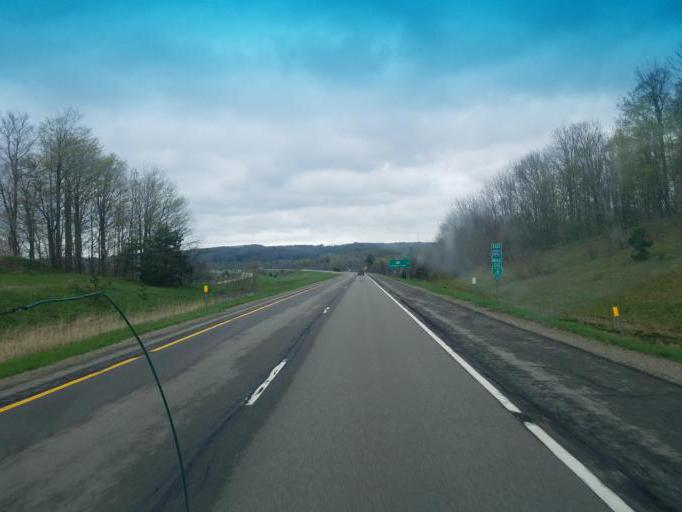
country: US
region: Pennsylvania
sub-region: Erie County
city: North East
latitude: 42.1295
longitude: -79.7501
